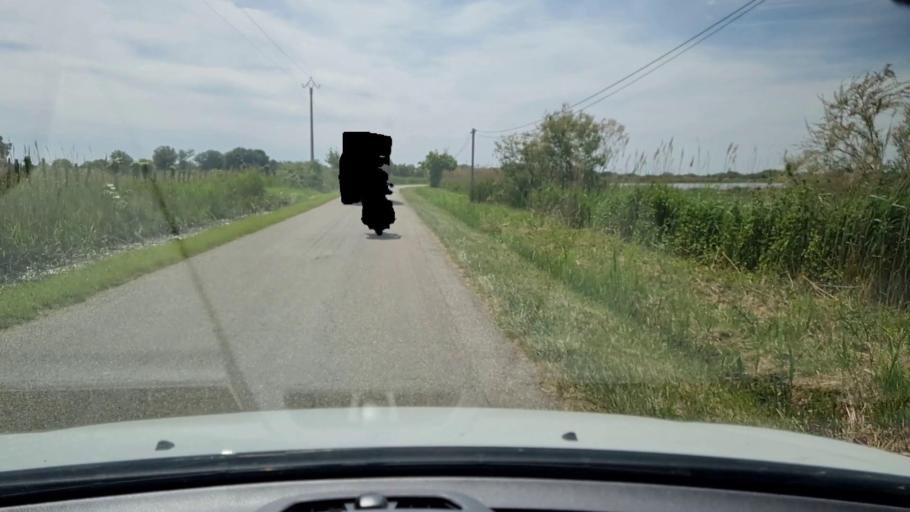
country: FR
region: Provence-Alpes-Cote d'Azur
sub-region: Departement des Bouches-du-Rhone
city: Saintes-Maries-de-la-Mer
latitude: 43.5500
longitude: 4.3634
